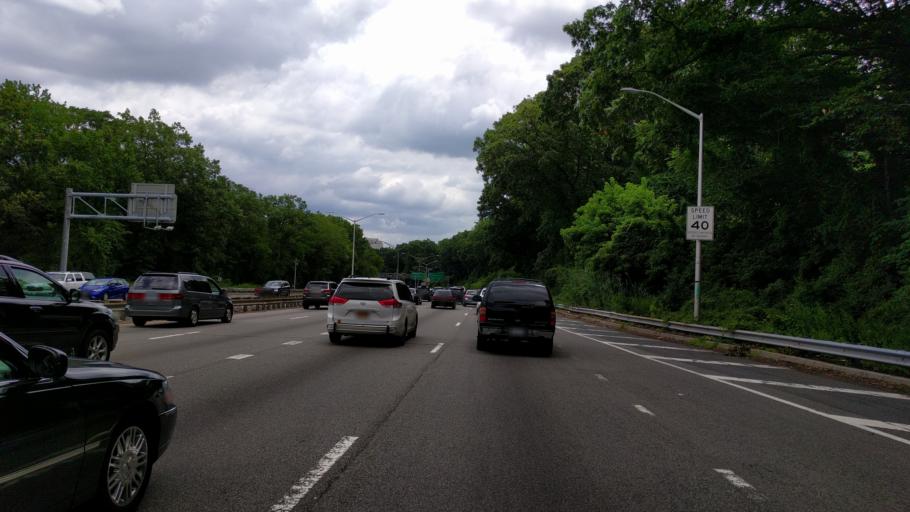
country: US
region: New York
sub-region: Queens County
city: Borough of Queens
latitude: 40.7196
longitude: -73.8338
